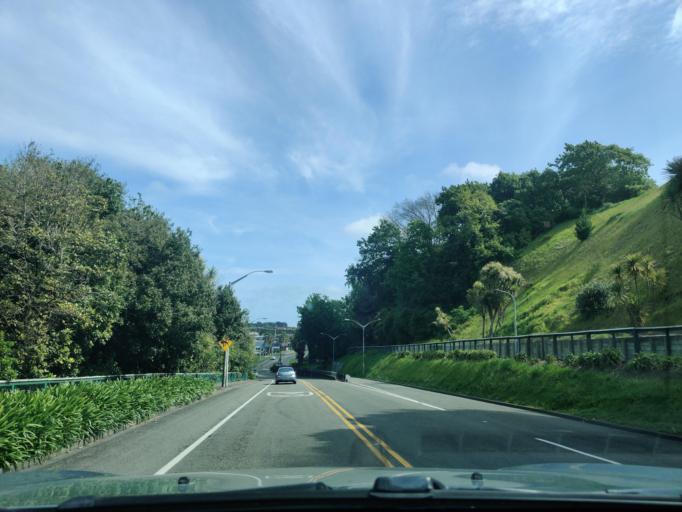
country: NZ
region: Manawatu-Wanganui
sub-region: Wanganui District
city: Wanganui
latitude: -39.9227
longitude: 175.0379
